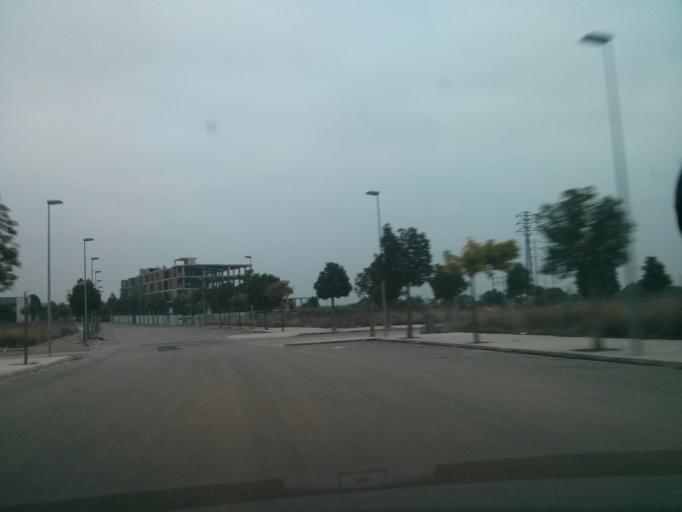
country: ES
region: Catalonia
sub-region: Provincia de Tarragona
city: El Vendrell
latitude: 41.2125
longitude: 1.5305
